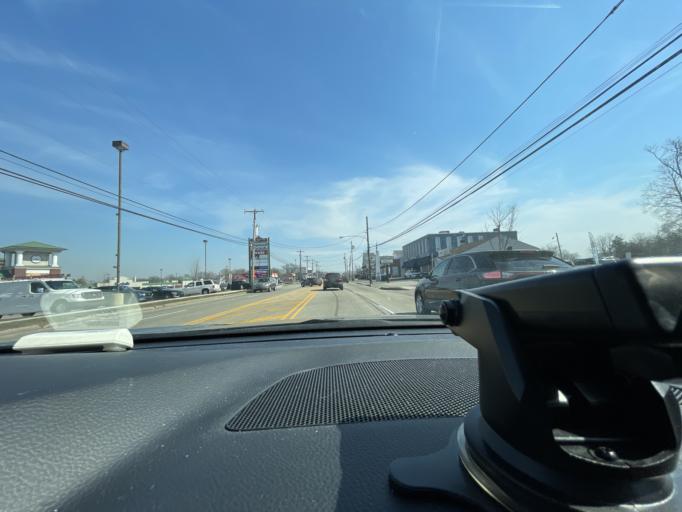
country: US
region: Pennsylvania
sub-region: Montgomery County
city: Plymouth Meeting
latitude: 40.0946
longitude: -75.2893
